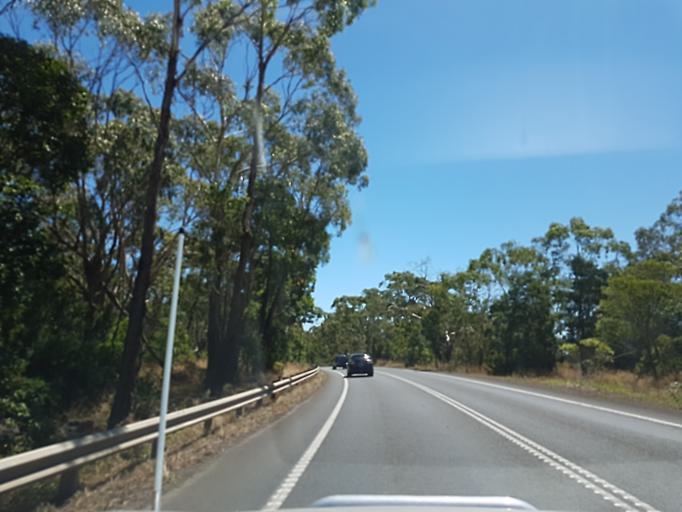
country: AU
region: Victoria
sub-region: Colac-Otway
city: Colac
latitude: -38.3473
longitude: 143.4122
